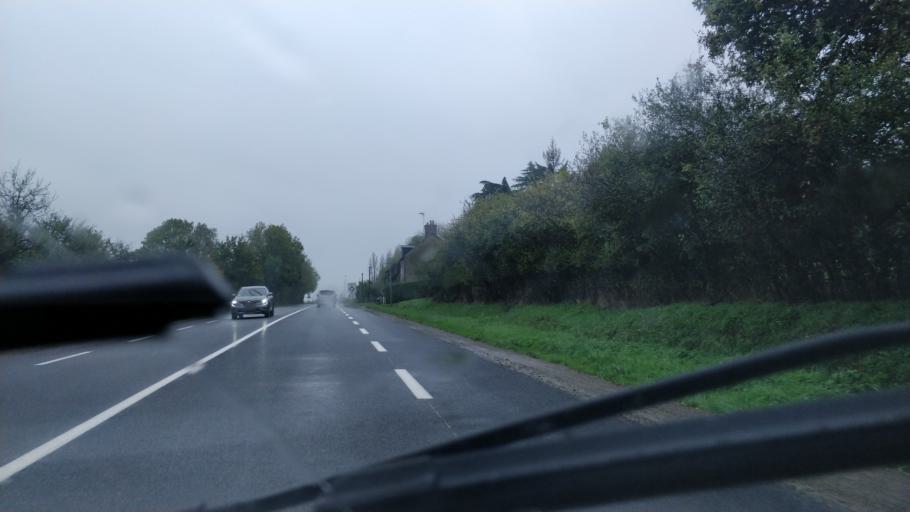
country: FR
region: Lower Normandy
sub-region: Departement de la Manche
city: Brehal
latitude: 48.8863
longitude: -1.5248
